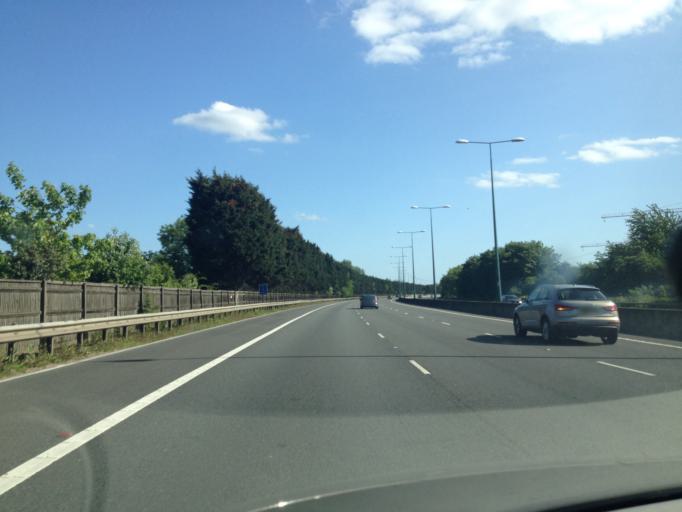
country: GB
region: England
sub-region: Greater London
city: Hendon
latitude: 51.5987
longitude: -0.2363
